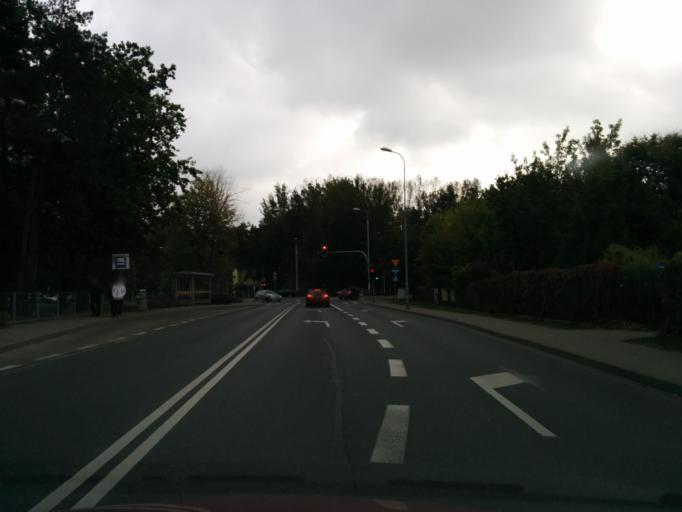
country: PL
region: Masovian Voivodeship
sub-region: Warszawa
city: Bemowo
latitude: 52.2494
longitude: 20.8969
